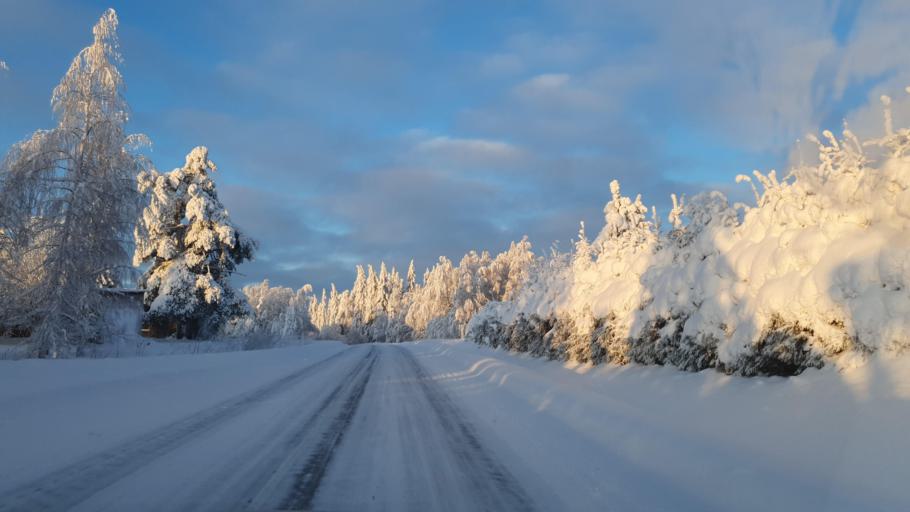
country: FI
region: Kainuu
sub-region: Kajaani
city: Vuokatti
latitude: 64.2715
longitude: 28.2381
